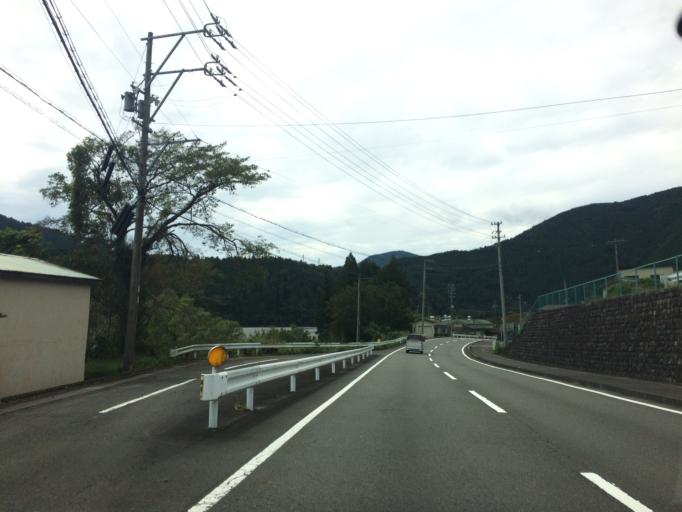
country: JP
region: Shizuoka
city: Kanaya
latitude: 35.0634
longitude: 138.1014
